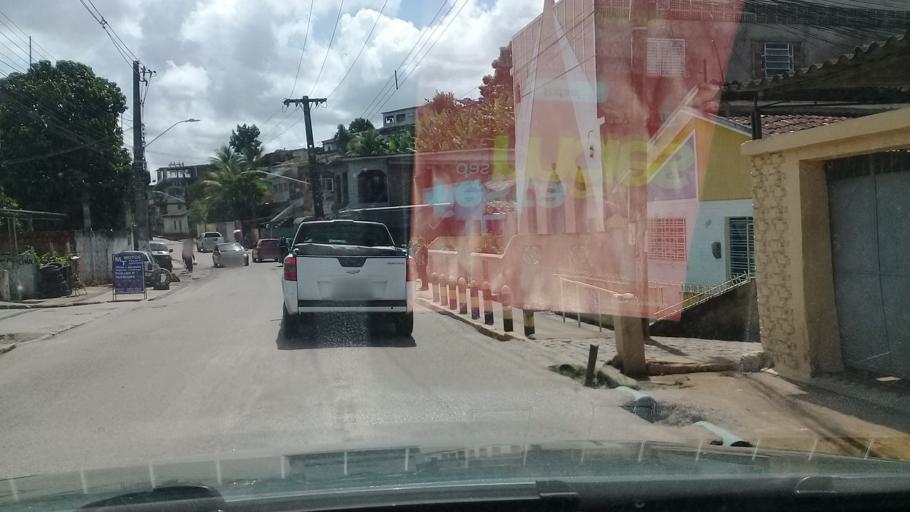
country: BR
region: Pernambuco
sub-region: Jaboatao Dos Guararapes
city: Jaboatao dos Guararapes
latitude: -8.1058
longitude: -35.0179
